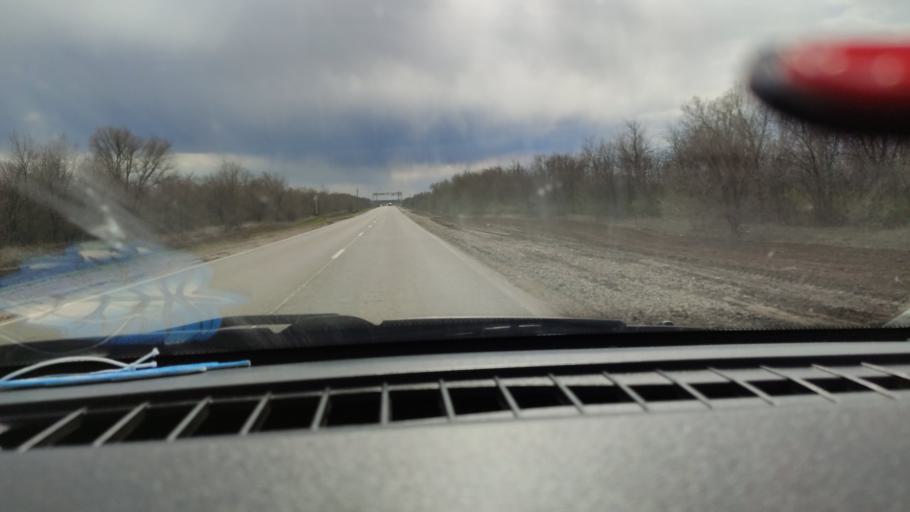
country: RU
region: Saratov
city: Privolzhskiy
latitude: 51.3222
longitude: 46.0268
